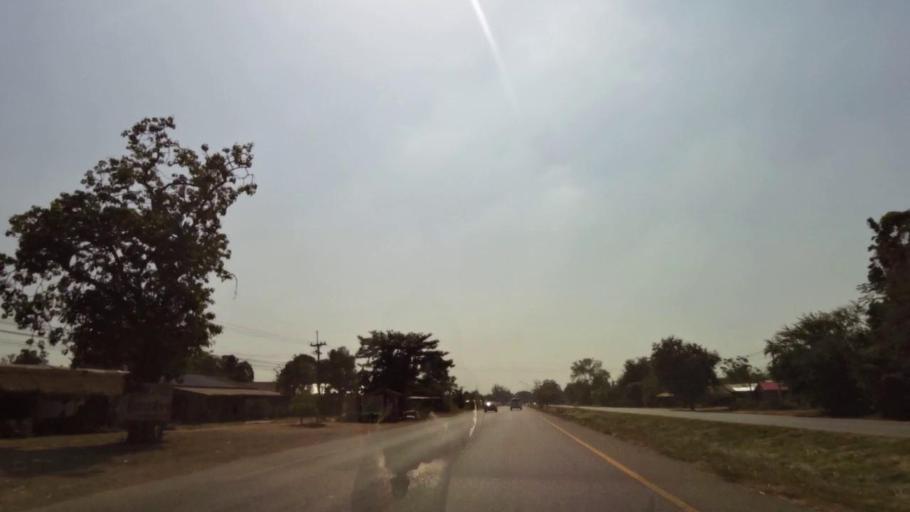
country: TH
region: Phichit
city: Wachira Barami
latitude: 16.3750
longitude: 100.1341
